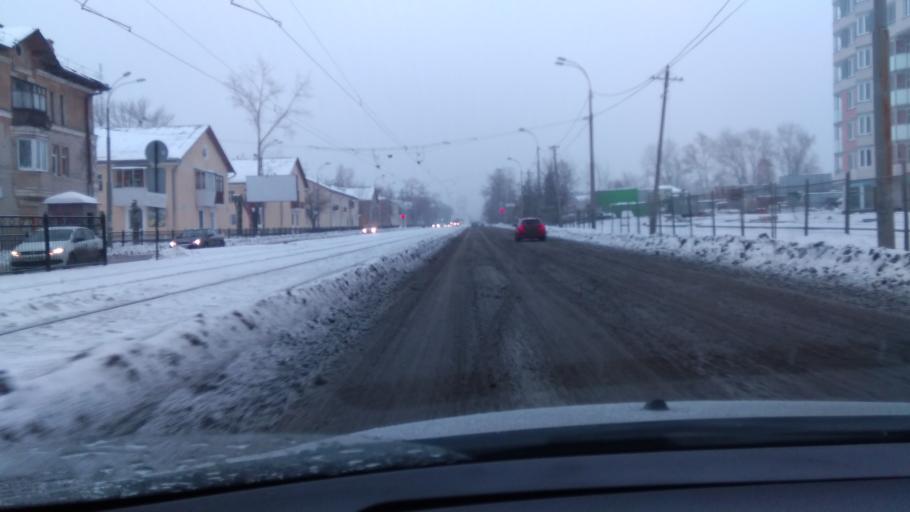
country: RU
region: Sverdlovsk
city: Yekaterinburg
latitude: 56.9016
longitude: 60.5829
